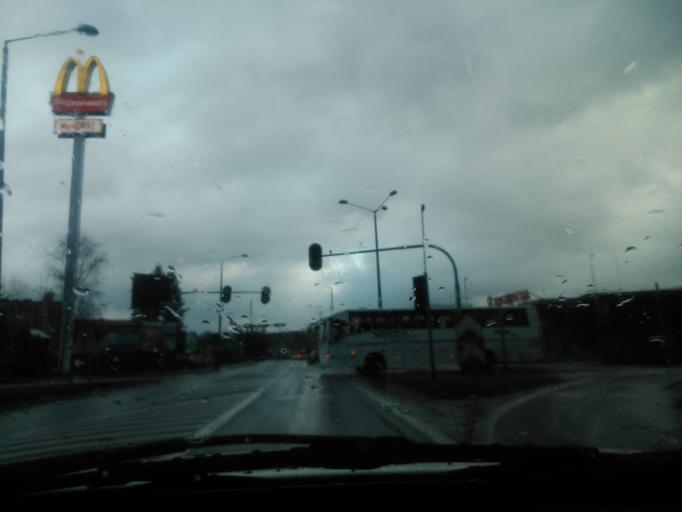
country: PL
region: Kujawsko-Pomorskie
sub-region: Powiat brodnicki
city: Brodnica
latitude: 53.2600
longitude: 19.3954
